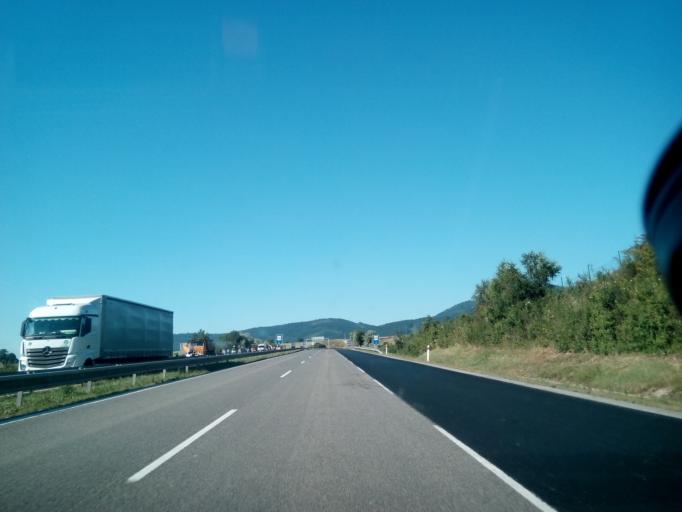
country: SK
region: Kosicky
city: Krompachy
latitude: 49.0030
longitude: 20.9324
